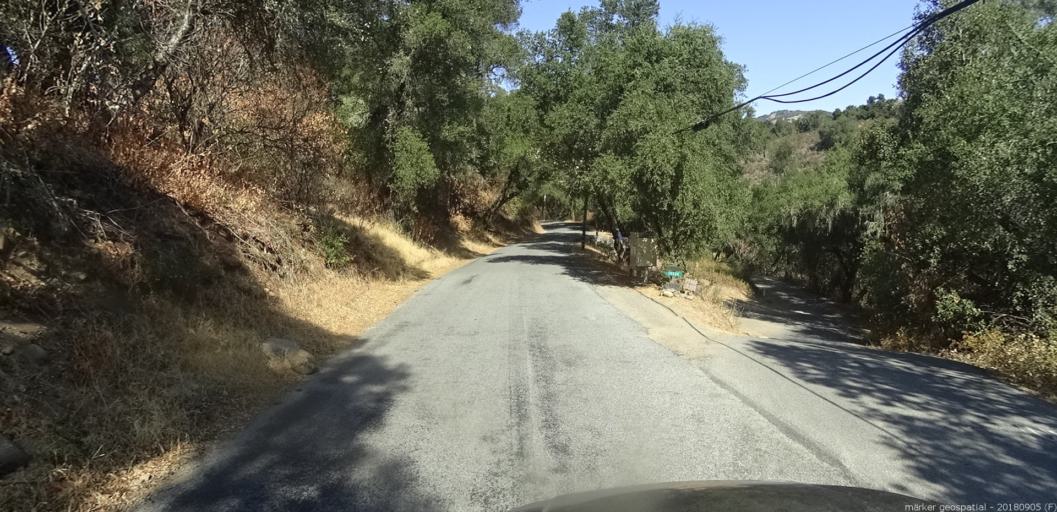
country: US
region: California
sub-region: Monterey County
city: Carmel Valley Village
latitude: 36.3943
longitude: -121.6410
